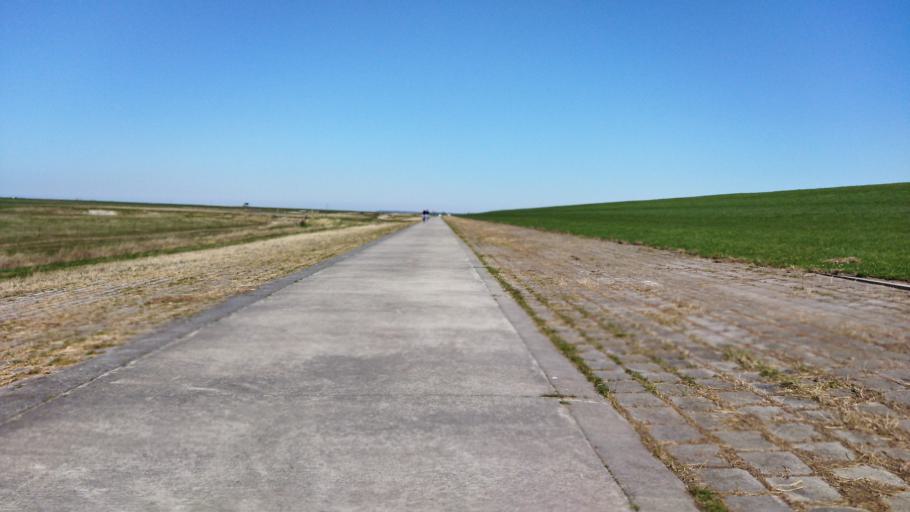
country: DE
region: Lower Saxony
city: Cappel
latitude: 53.7577
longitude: 8.5332
